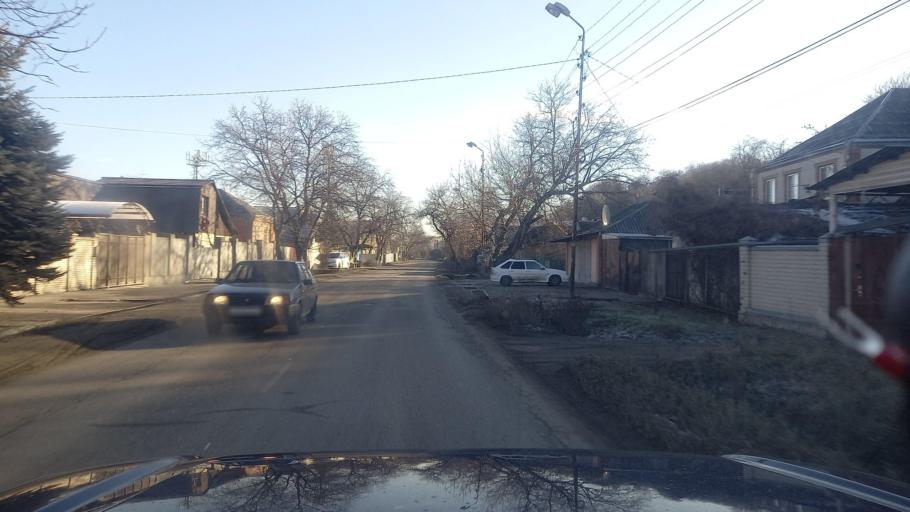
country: RU
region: Stavropol'skiy
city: Svobody
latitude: 44.0238
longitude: 43.0576
